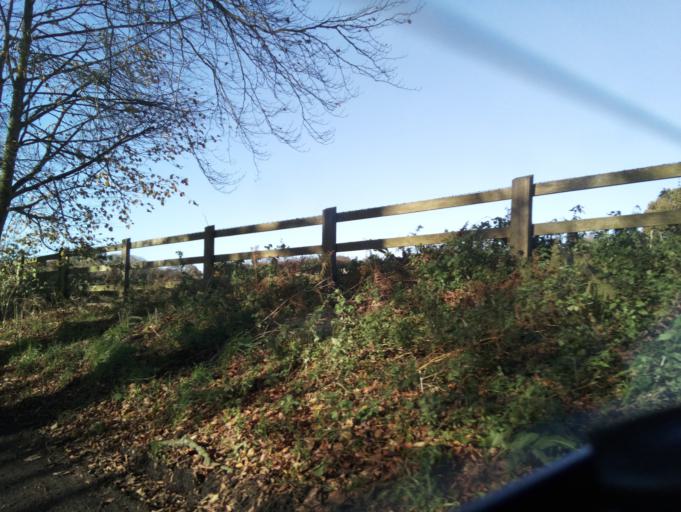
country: GB
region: England
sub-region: Somerset
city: Yeovil
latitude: 50.9315
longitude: -2.6265
